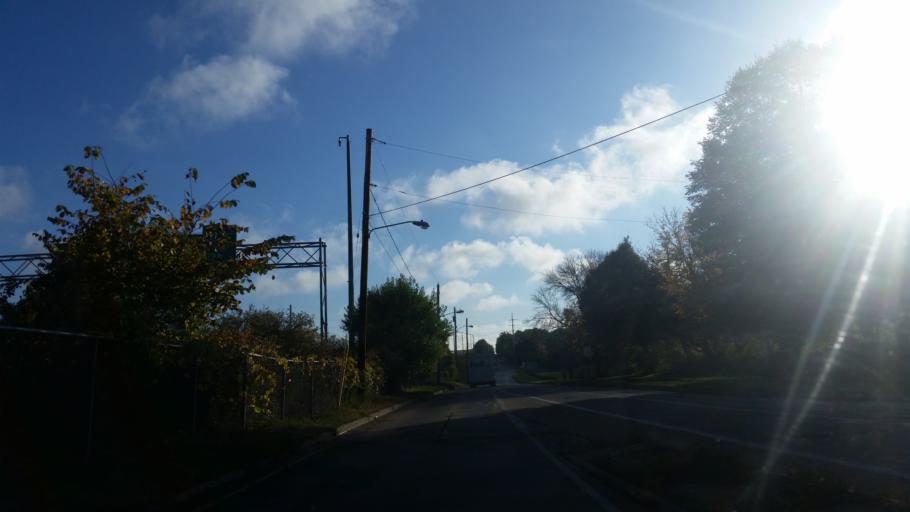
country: US
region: Ohio
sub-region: Summit County
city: Akron
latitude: 41.0615
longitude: -81.5463
